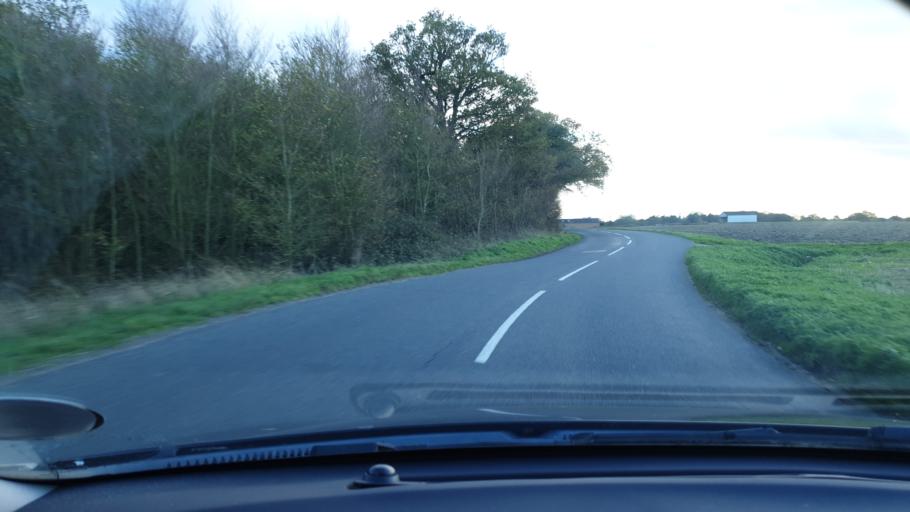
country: GB
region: England
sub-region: Essex
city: Mistley
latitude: 51.9072
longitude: 1.1438
